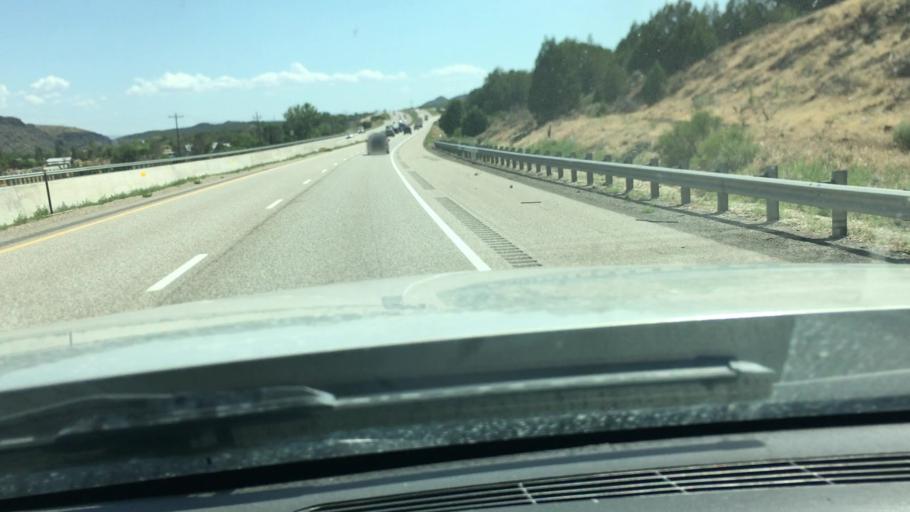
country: US
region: Utah
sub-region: Washington County
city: Toquerville
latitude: 37.3491
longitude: -113.2694
